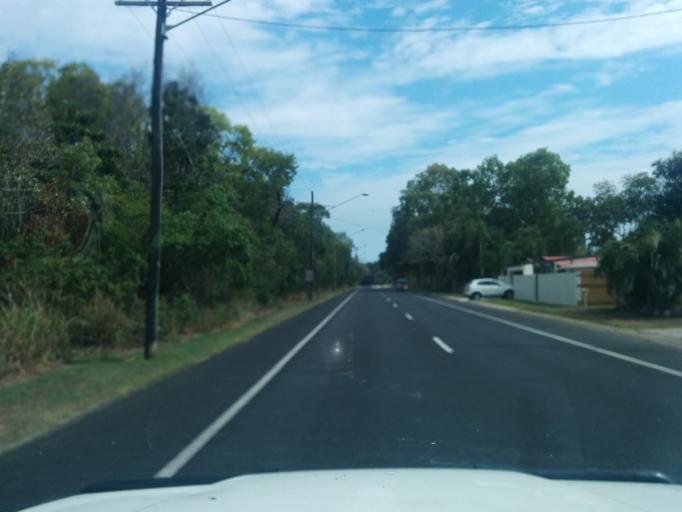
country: AU
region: Queensland
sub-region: Cairns
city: Yorkeys Knob
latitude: -16.8445
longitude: 145.7351
